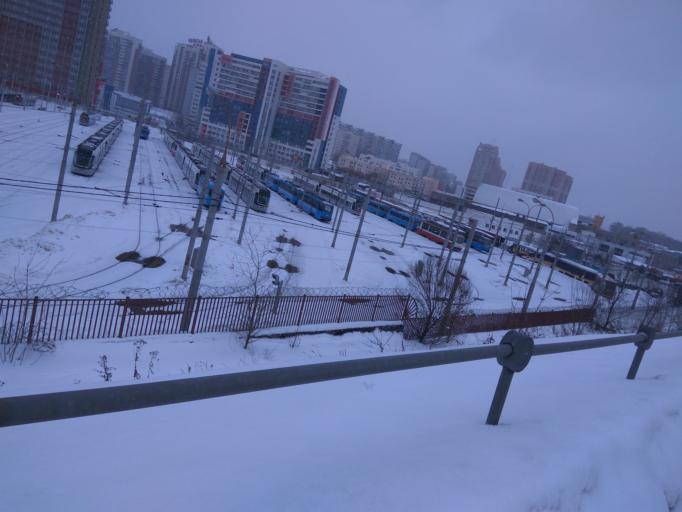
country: RU
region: Moscow
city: Rublevo
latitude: 55.7932
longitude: 37.3843
